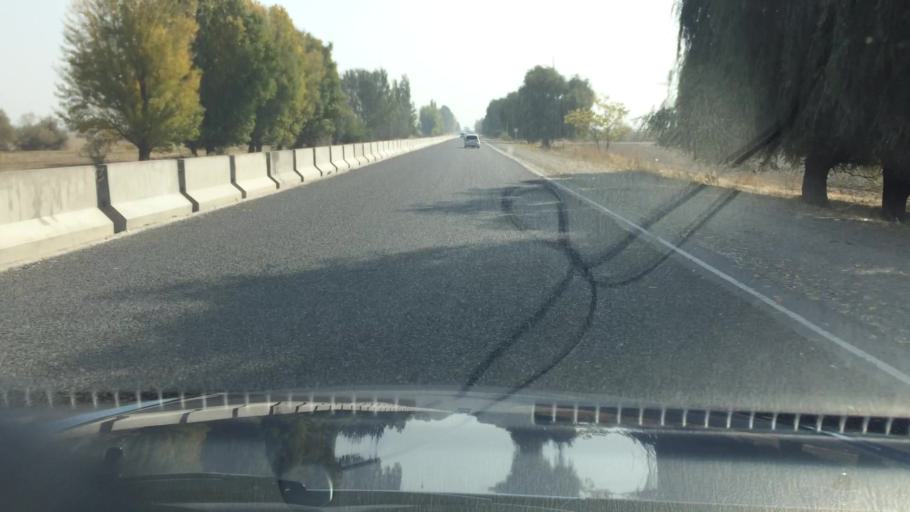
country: KG
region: Chuy
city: Kant
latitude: 42.9687
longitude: 74.9061
